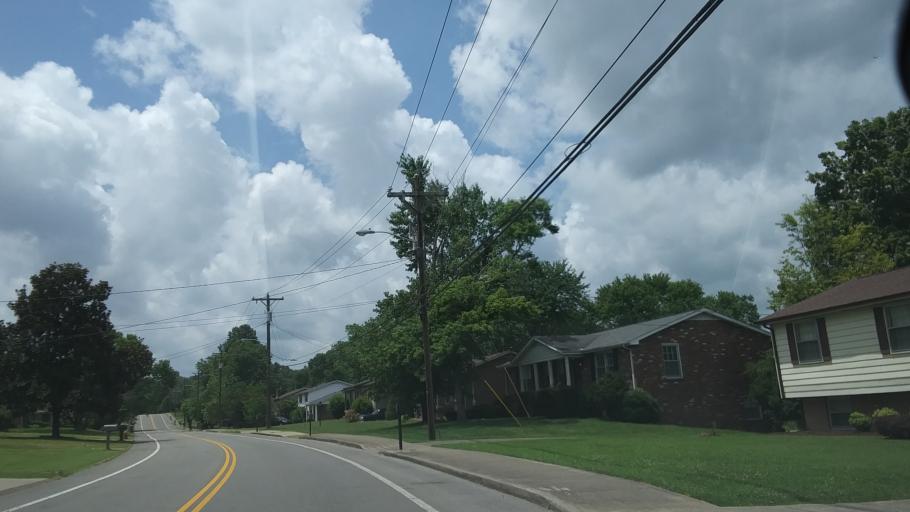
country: US
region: Tennessee
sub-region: Davidson County
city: Belle Meade
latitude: 36.1395
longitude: -86.8897
